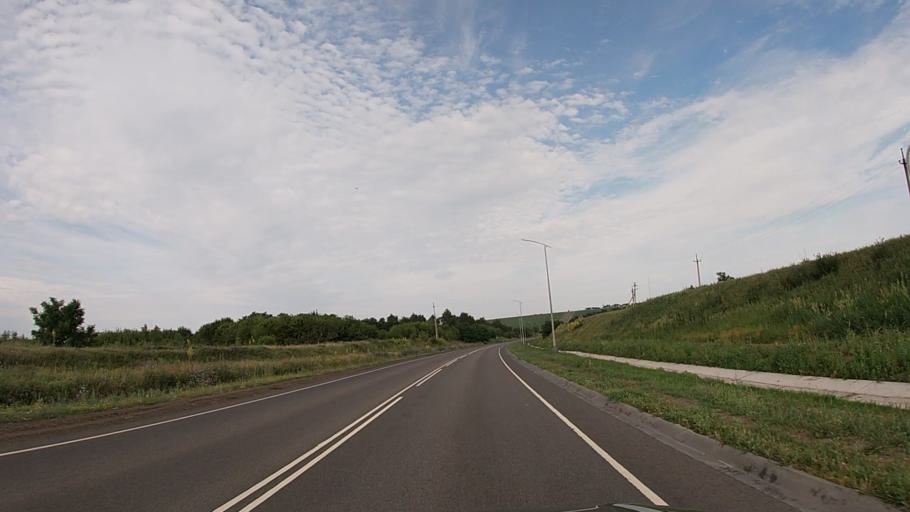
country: RU
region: Belgorod
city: Severnyy
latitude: 50.6645
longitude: 36.5278
